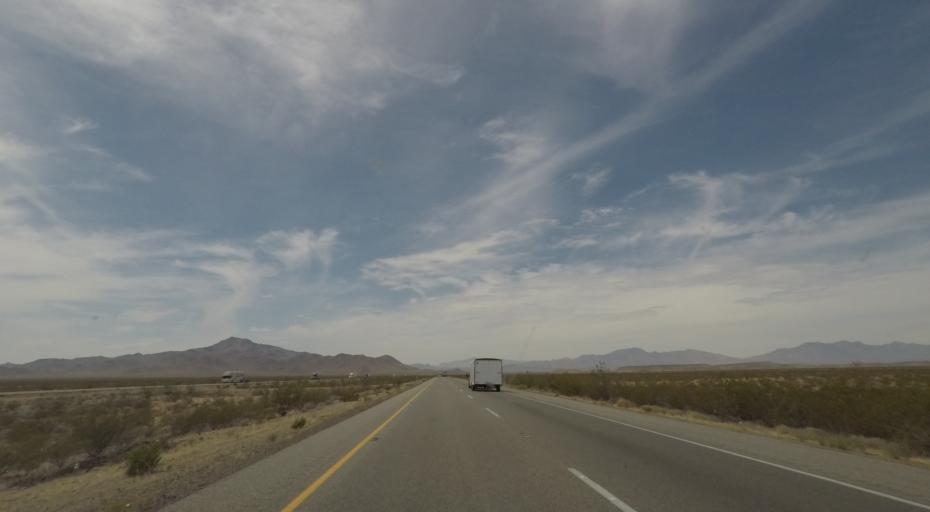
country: US
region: California
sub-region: San Bernardino County
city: Needles
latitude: 34.8057
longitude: -115.2657
